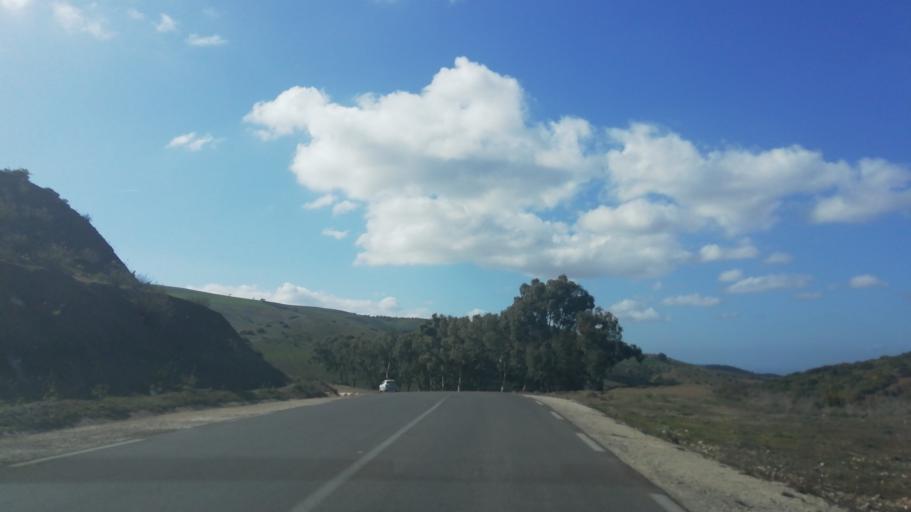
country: DZ
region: Relizane
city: Relizane
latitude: 36.0820
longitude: 0.4883
